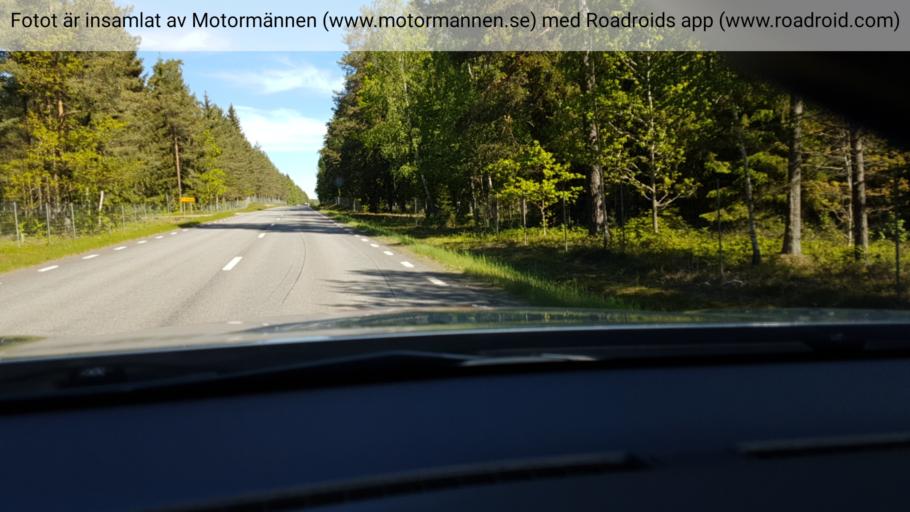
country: SE
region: Vaestra Goetaland
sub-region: Hjo Kommun
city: Hjo
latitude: 58.3703
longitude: 14.3519
